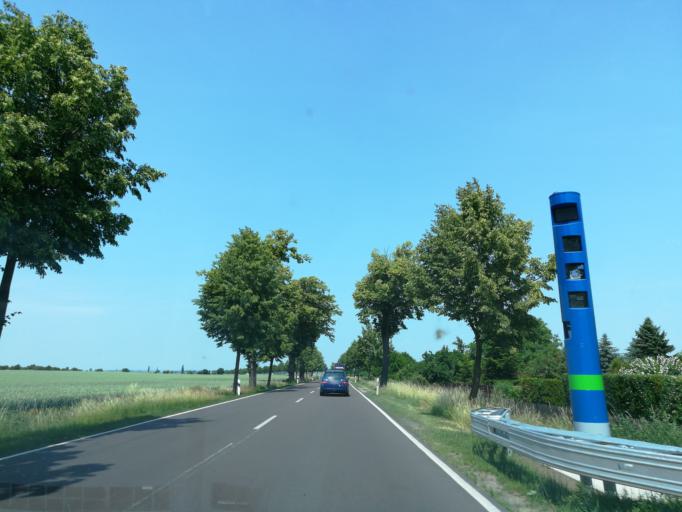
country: DE
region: Saxony-Anhalt
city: Schneidlingen
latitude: 51.8987
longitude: 11.4400
